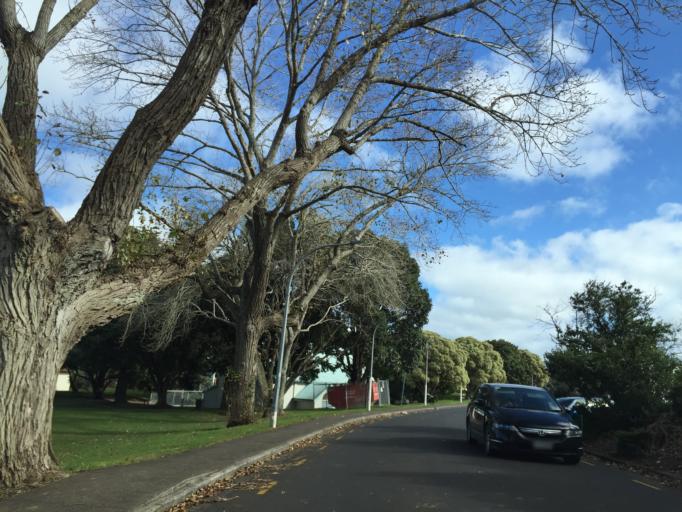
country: NZ
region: Auckland
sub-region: Auckland
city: Auckland
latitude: -36.9074
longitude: 174.7576
